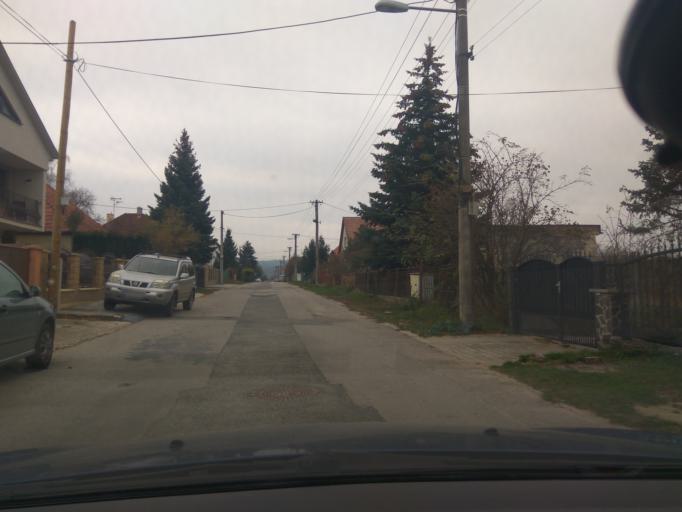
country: SK
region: Trnavsky
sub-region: Okres Trnava
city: Piestany
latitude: 48.6019
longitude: 17.8566
